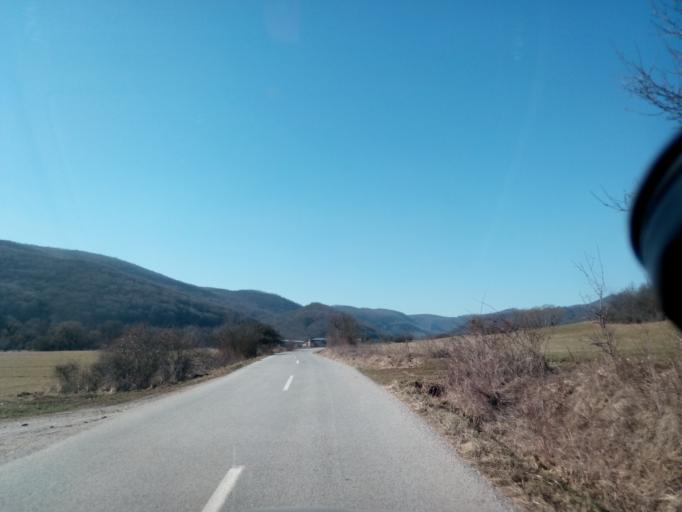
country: SK
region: Kosicky
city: Roznava
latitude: 48.5630
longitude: 20.6270
